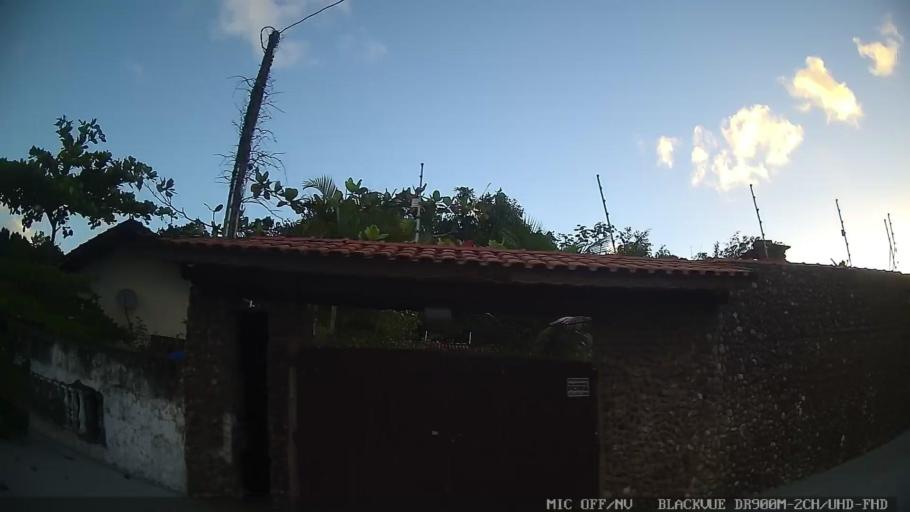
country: BR
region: Sao Paulo
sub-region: Itanhaem
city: Itanhaem
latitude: -24.1443
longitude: -46.7306
